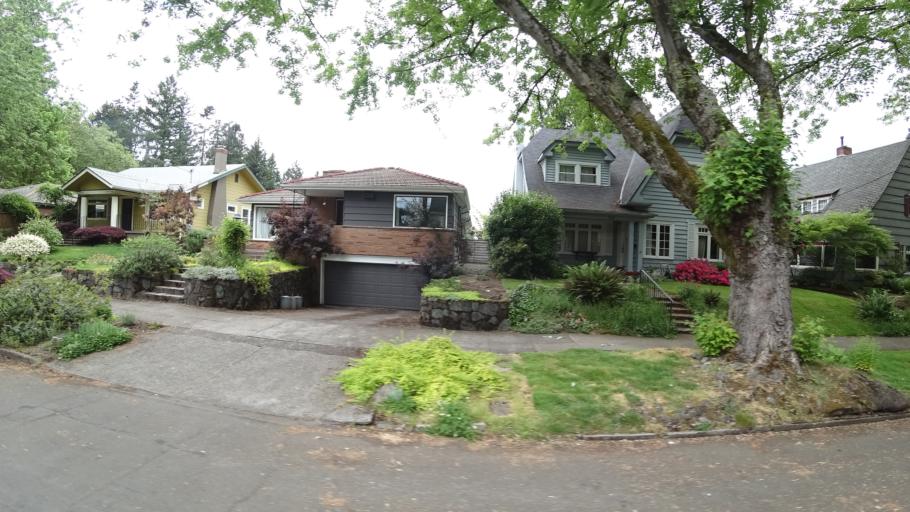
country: US
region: Oregon
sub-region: Multnomah County
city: Portland
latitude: 45.5203
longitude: -122.6222
